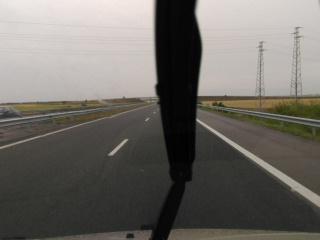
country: BG
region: Stara Zagora
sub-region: Obshtina Stara Zagora
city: Stara Zagora
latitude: 42.3635
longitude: 25.7699
